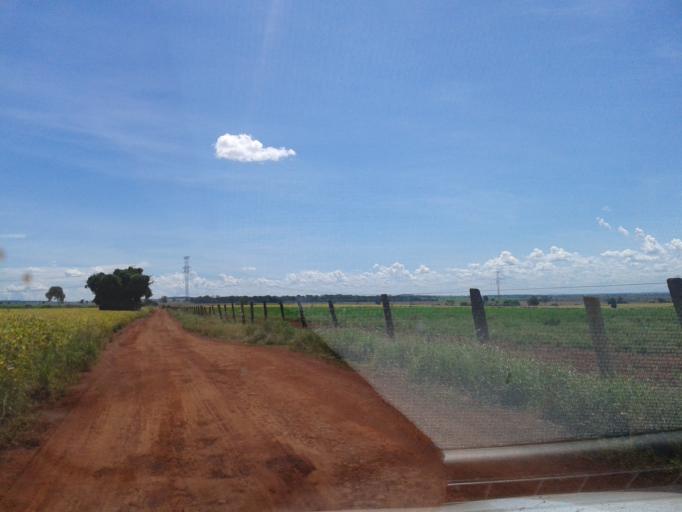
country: BR
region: Minas Gerais
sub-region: Capinopolis
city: Capinopolis
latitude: -18.7041
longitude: -49.7787
